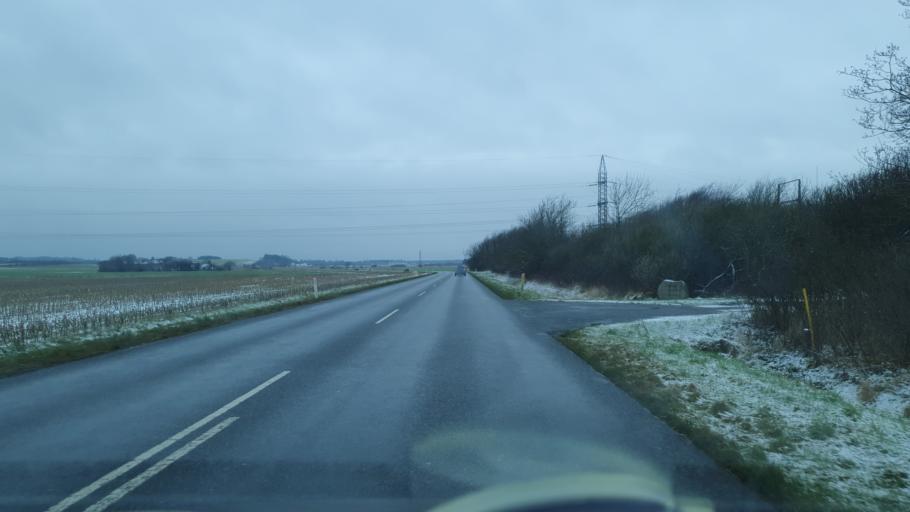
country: DK
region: North Denmark
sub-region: Jammerbugt Kommune
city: Brovst
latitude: 57.1130
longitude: 9.5007
